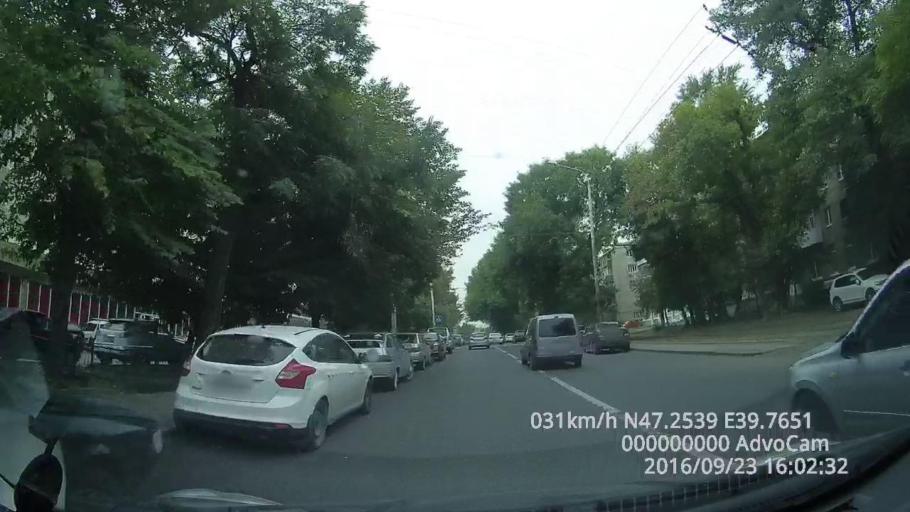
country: RU
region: Rostov
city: Imeni Chkalova
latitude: 47.2538
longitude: 39.7651
